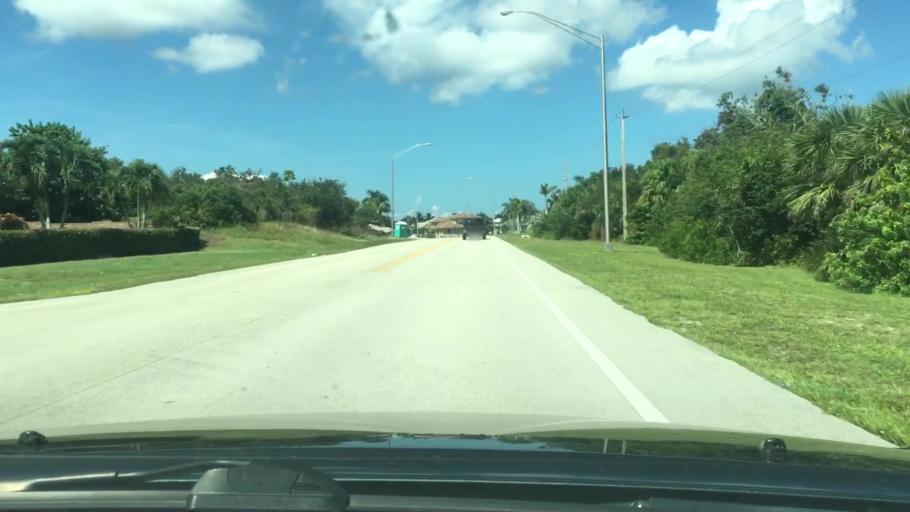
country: US
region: Florida
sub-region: Collier County
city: Marco
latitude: 25.9383
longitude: -81.6876
